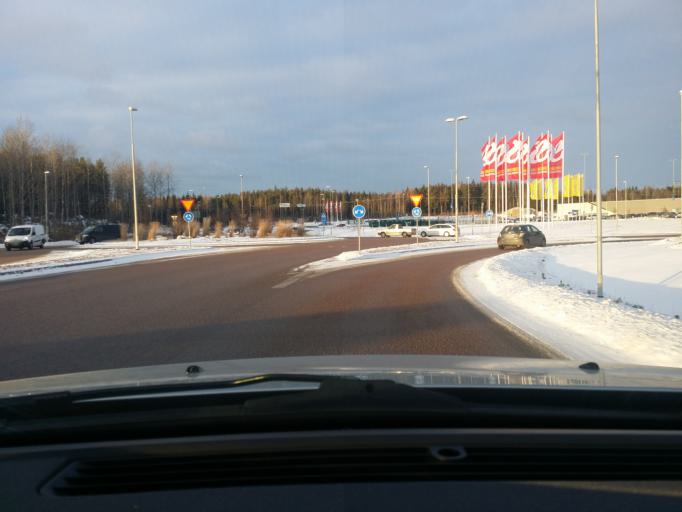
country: SE
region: Vaestmanland
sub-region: Vasteras
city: Vasteras
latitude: 59.6070
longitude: 16.4507
